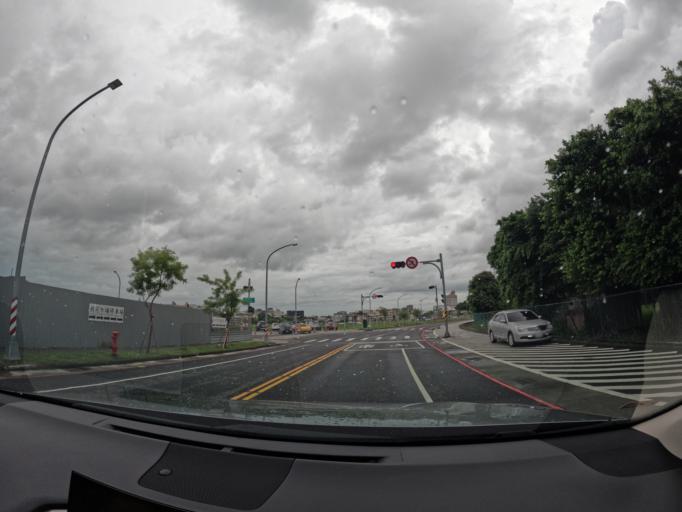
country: TW
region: Taiwan
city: Fengshan
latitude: 22.6320
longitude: 120.3731
